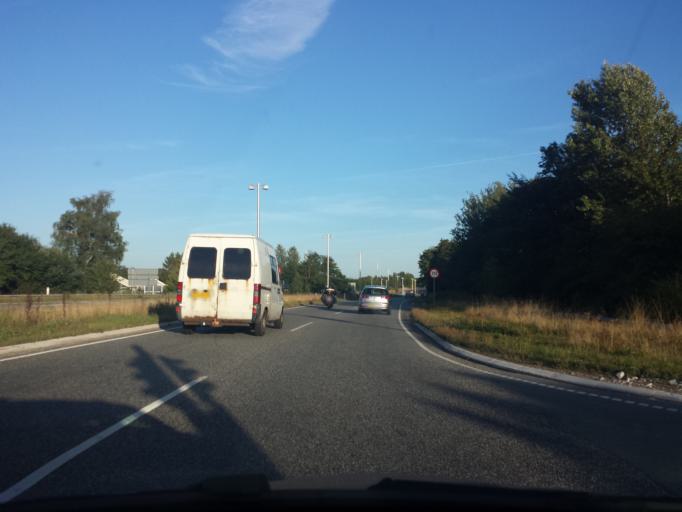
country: DK
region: Capital Region
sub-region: Egedal Kommune
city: Olstykke
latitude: 55.7838
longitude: 12.1572
